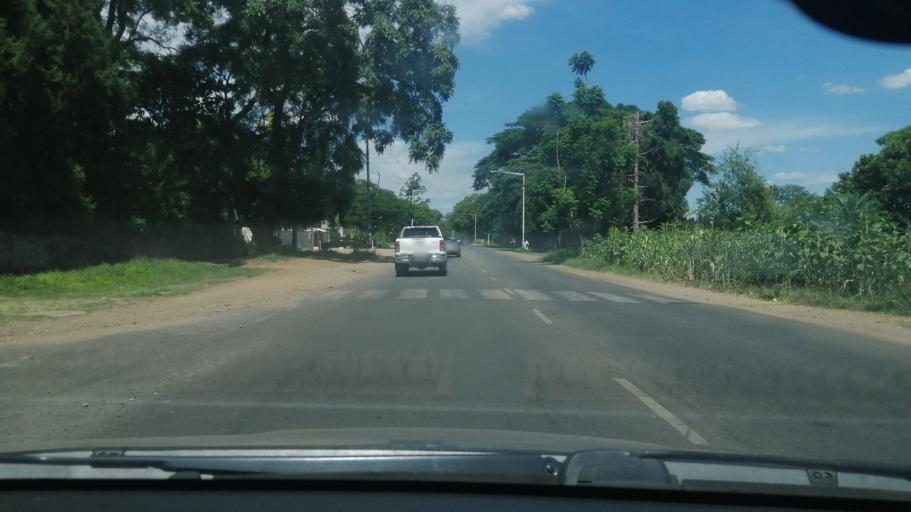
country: ZW
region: Harare
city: Harare
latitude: -17.8188
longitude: 31.0610
